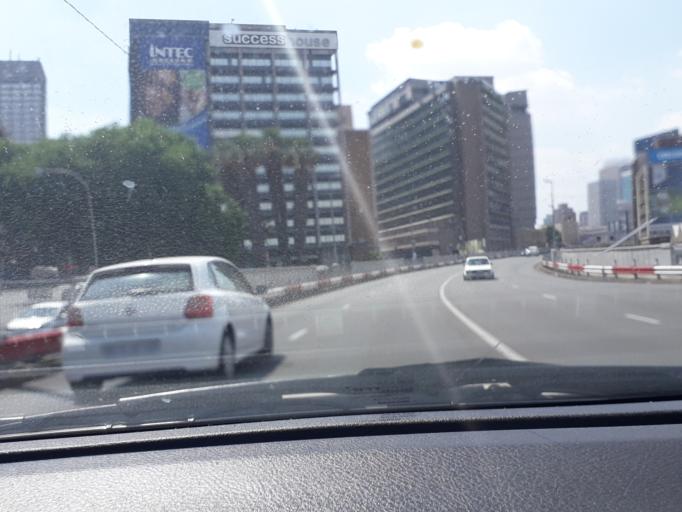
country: ZA
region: Gauteng
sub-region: City of Johannesburg Metropolitan Municipality
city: Johannesburg
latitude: -26.1953
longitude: 28.0350
